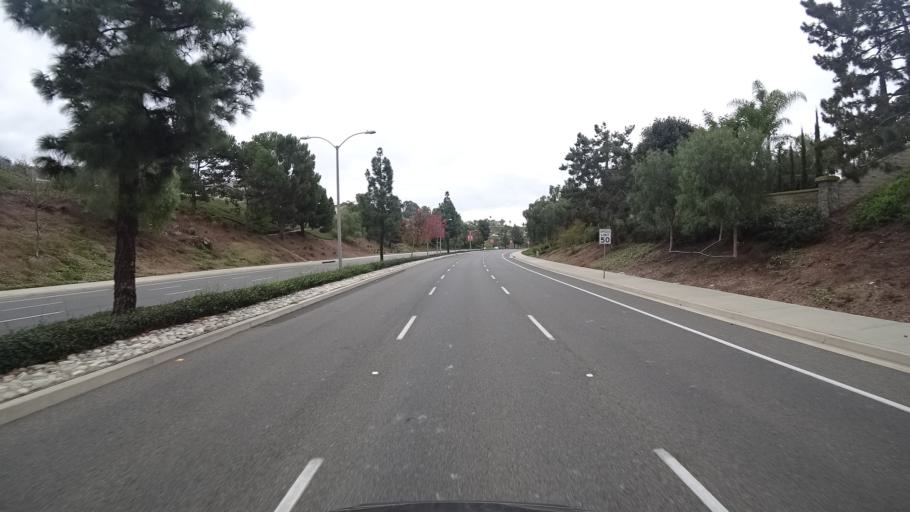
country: US
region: California
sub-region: Orange County
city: Laguna Niguel
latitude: 33.4988
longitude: -117.6929
